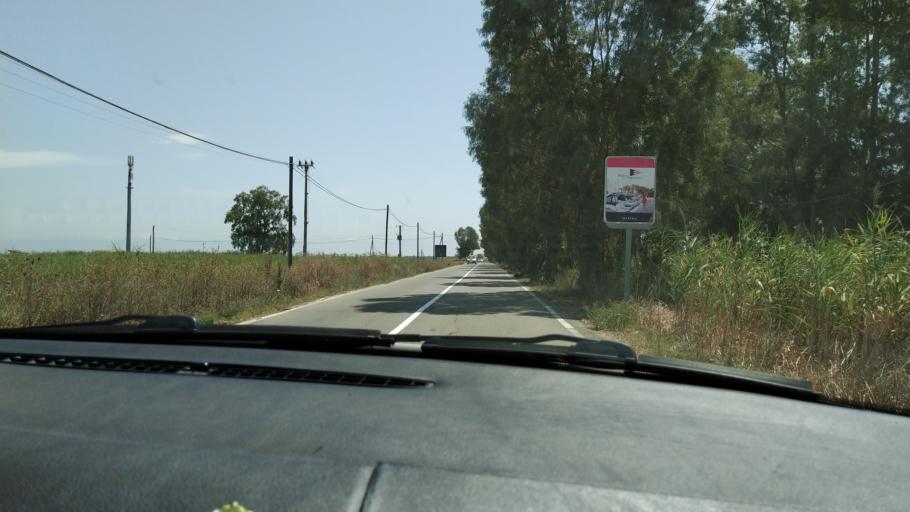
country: IT
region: Basilicate
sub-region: Provincia di Matera
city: Marconia
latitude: 40.3392
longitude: 16.7655
